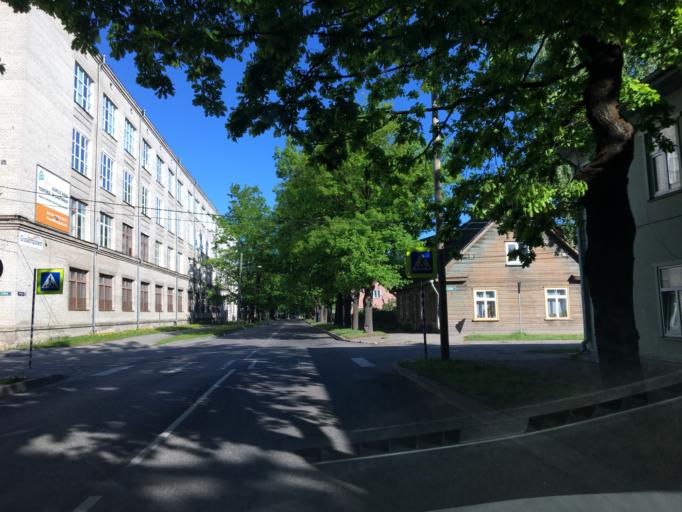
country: EE
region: Tartu
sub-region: Tartu linn
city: Tartu
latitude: 58.3923
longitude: 26.7212
